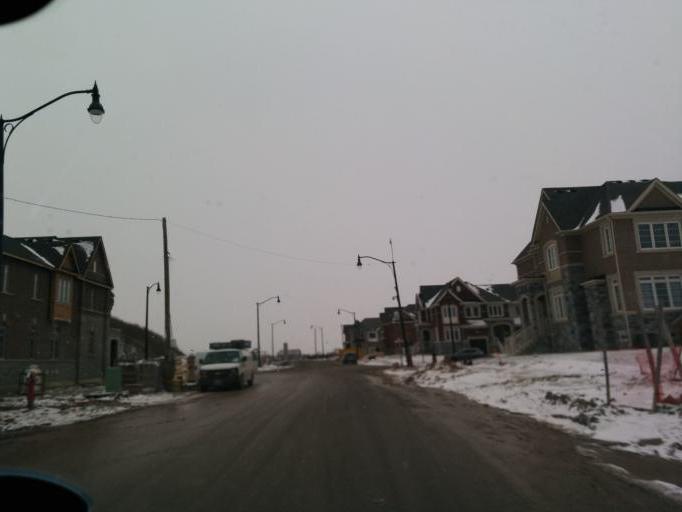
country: CA
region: Ontario
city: Brampton
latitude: 43.6298
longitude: -79.7878
